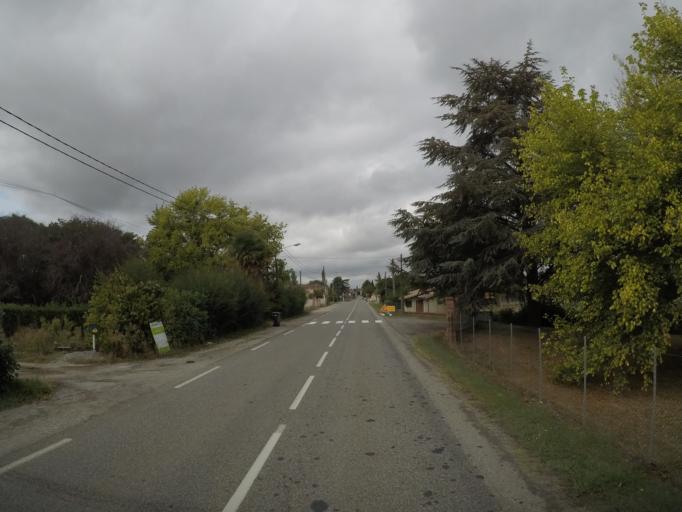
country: FR
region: Midi-Pyrenees
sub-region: Departement de la Haute-Garonne
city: Gaillac-Toulza
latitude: 43.1697
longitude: 1.4125
